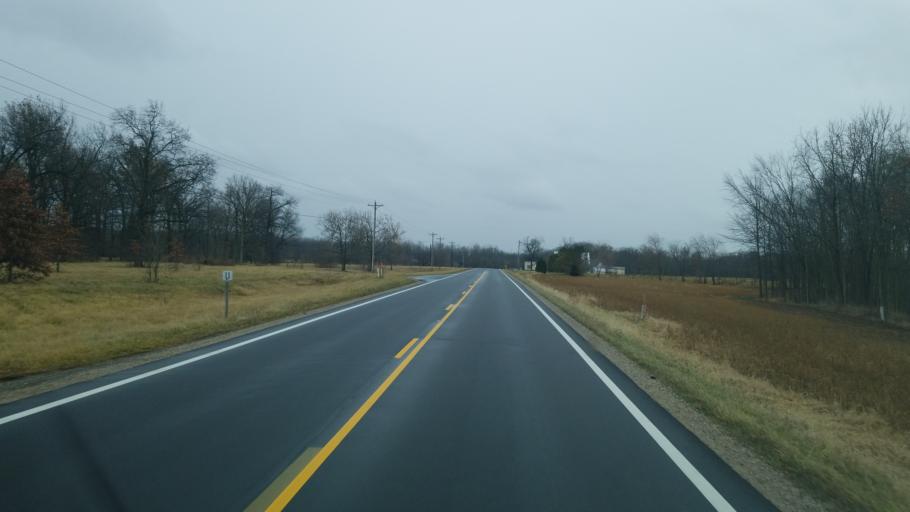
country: US
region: Ohio
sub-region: Union County
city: Richwood
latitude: 40.3900
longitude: -83.4090
